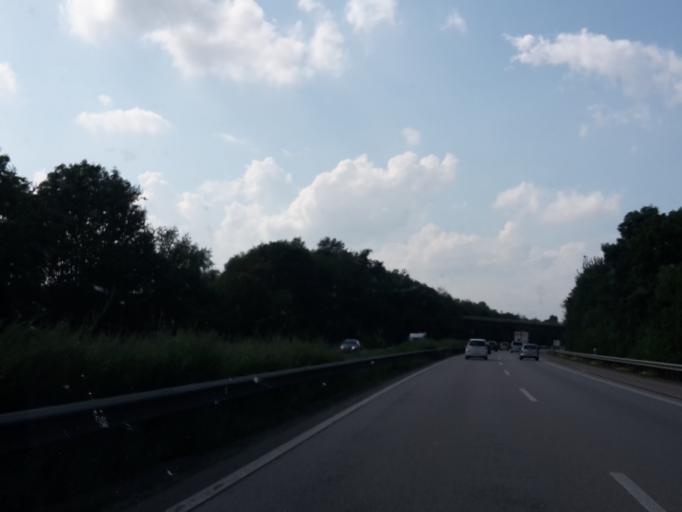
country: DE
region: Rheinland-Pfalz
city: Gau-Bickelheim
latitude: 49.8303
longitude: 8.0236
